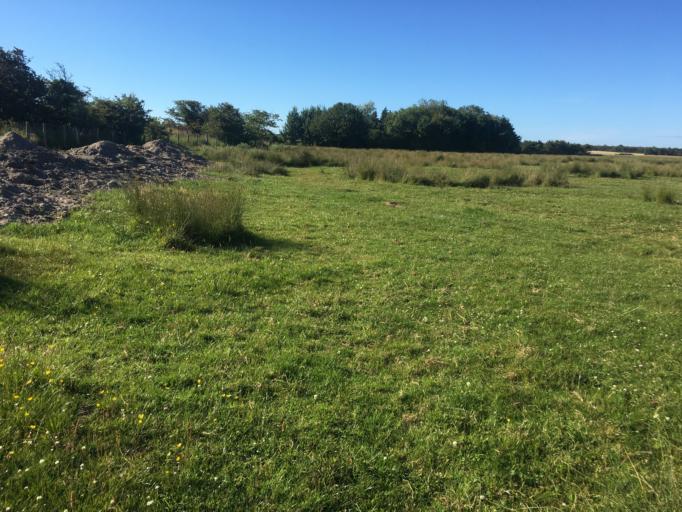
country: GB
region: England
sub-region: Northumberland
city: North Sunderland
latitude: 55.5669
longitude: -1.6531
